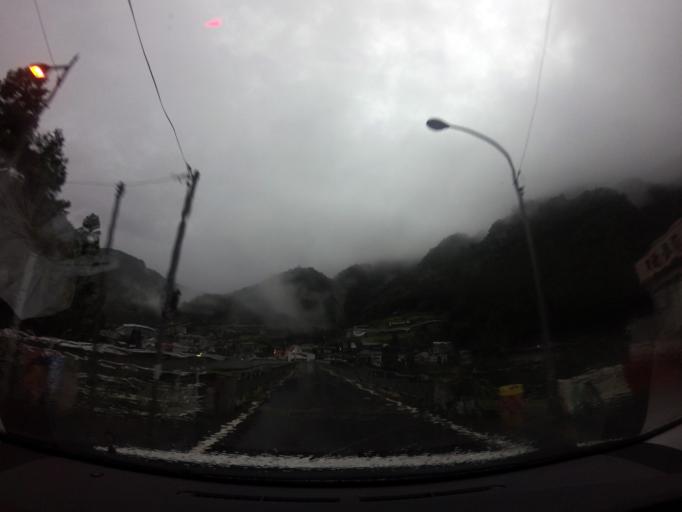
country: JP
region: Wakayama
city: Shingu
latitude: 33.9467
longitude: 135.8047
